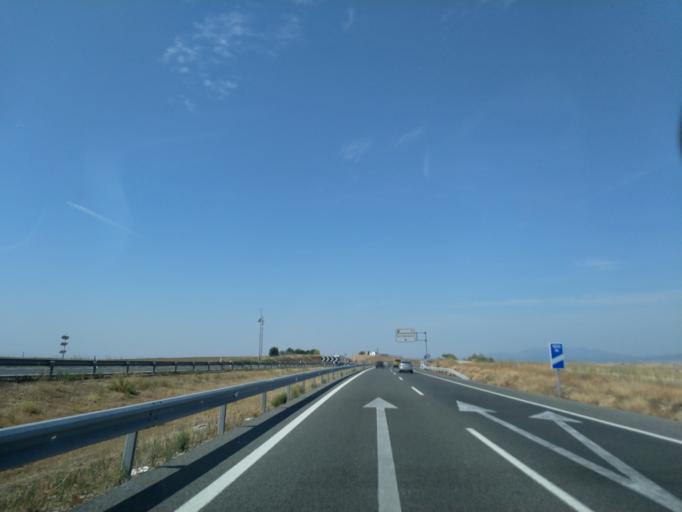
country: ES
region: Castille-La Mancha
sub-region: Province of Toledo
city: Quismondo
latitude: 40.1150
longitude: -4.3066
